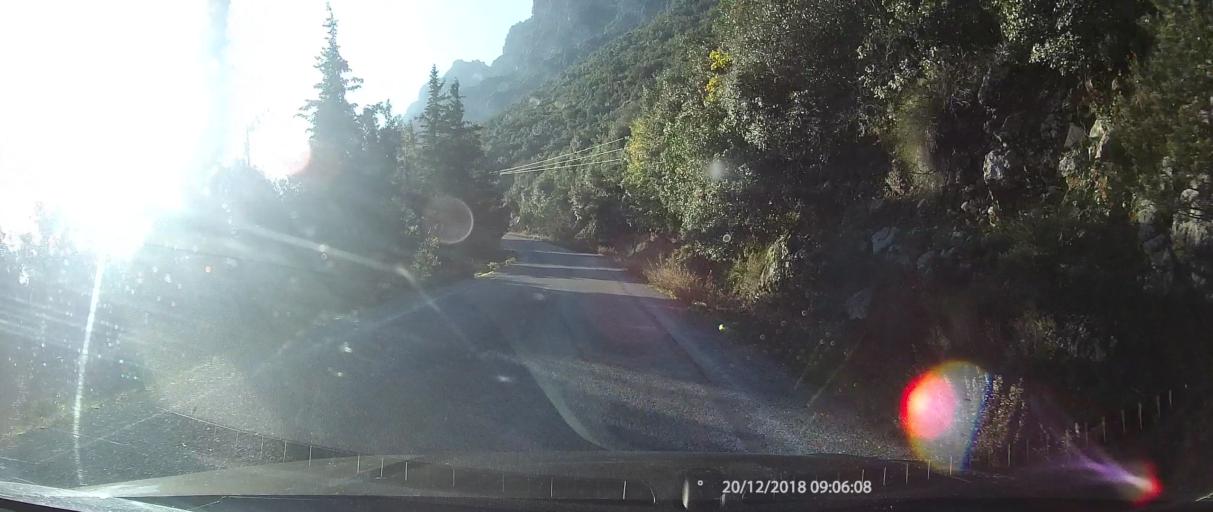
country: GR
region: Peloponnese
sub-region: Nomos Lakonias
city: Sykea
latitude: 36.9360
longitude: 22.9986
